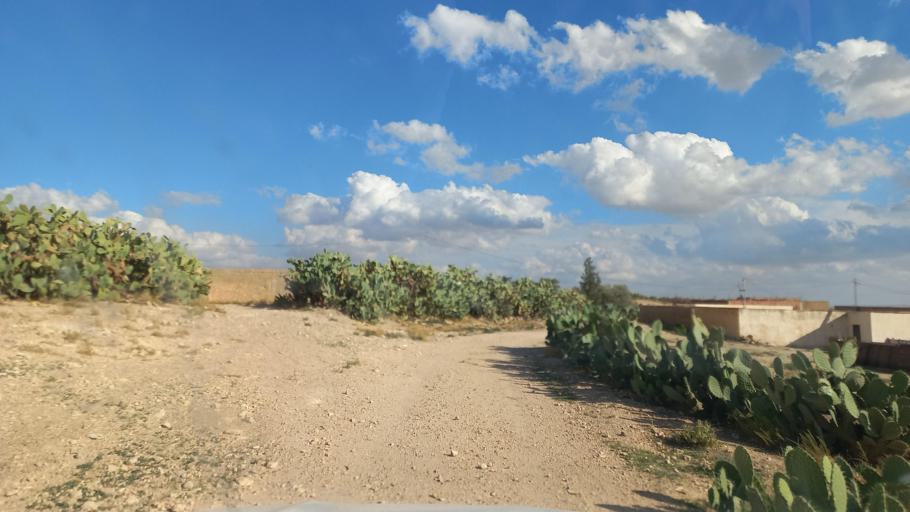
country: TN
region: Al Qasrayn
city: Sbiba
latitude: 35.3922
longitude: 9.0418
